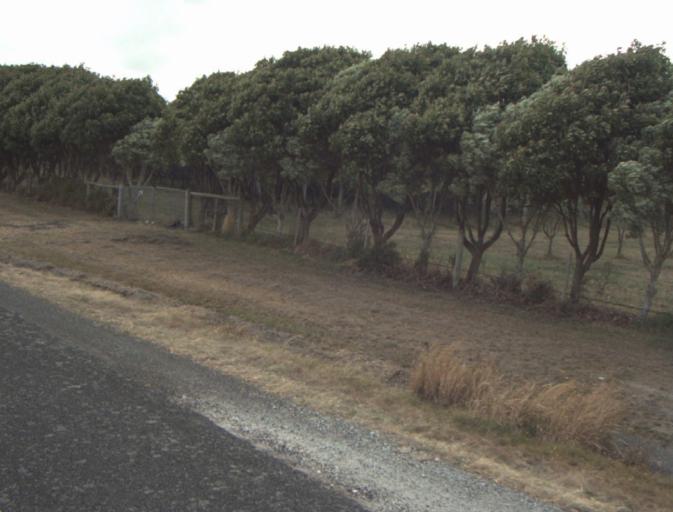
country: AU
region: Tasmania
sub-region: Launceston
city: Mayfield
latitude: -41.3301
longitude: 147.0576
